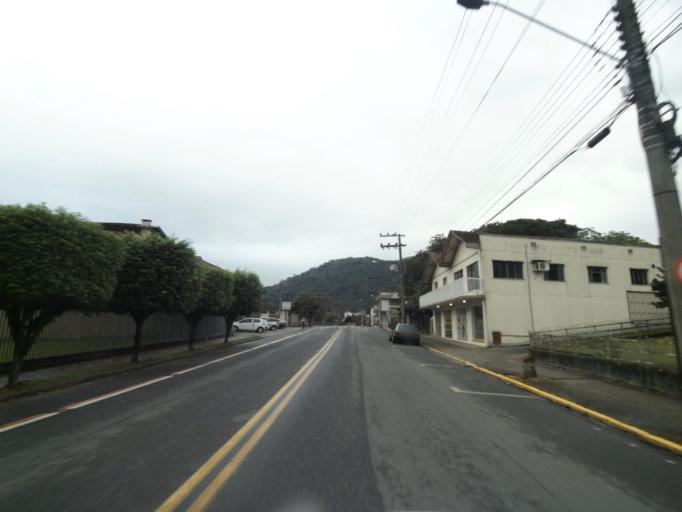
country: BR
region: Santa Catarina
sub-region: Pomerode
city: Pomerode
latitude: -26.7281
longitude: -49.1746
